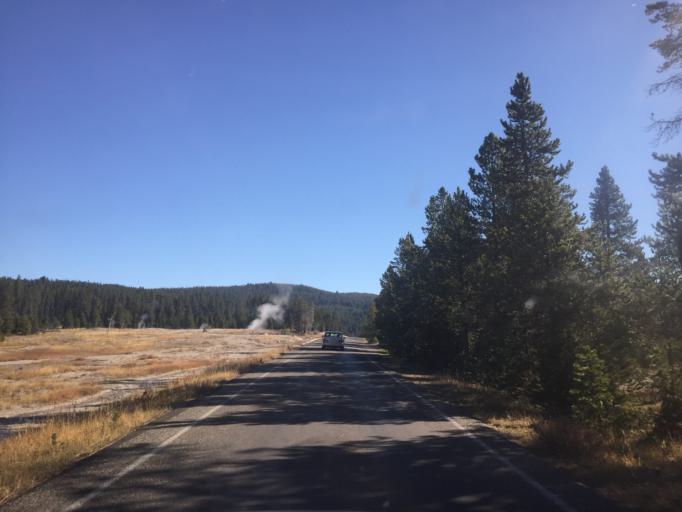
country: US
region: Montana
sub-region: Gallatin County
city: West Yellowstone
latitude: 44.5425
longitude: -110.7973
